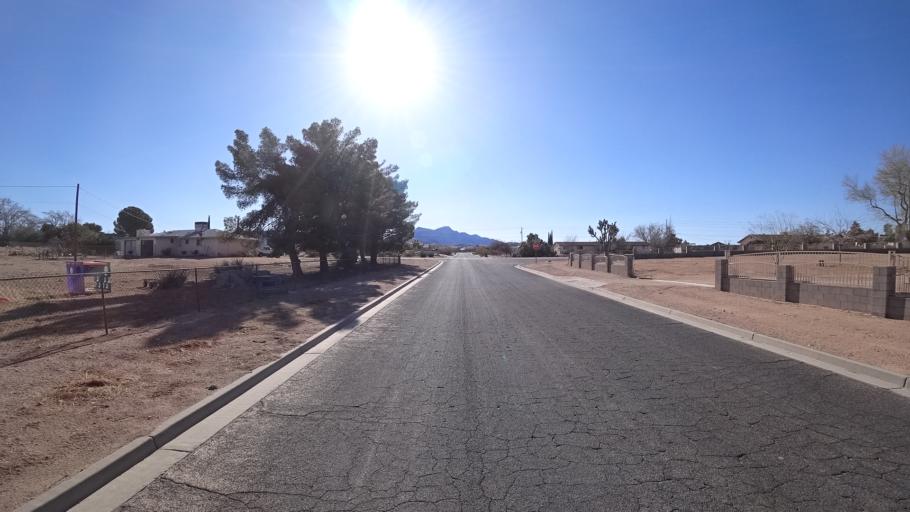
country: US
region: Arizona
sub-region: Mohave County
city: Kingman
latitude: 35.1981
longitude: -114.0060
